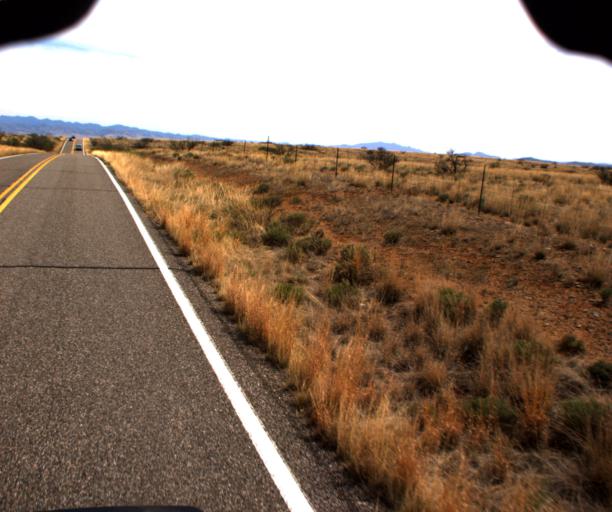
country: US
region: Arizona
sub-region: Cochise County
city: Willcox
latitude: 32.1380
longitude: -109.5630
